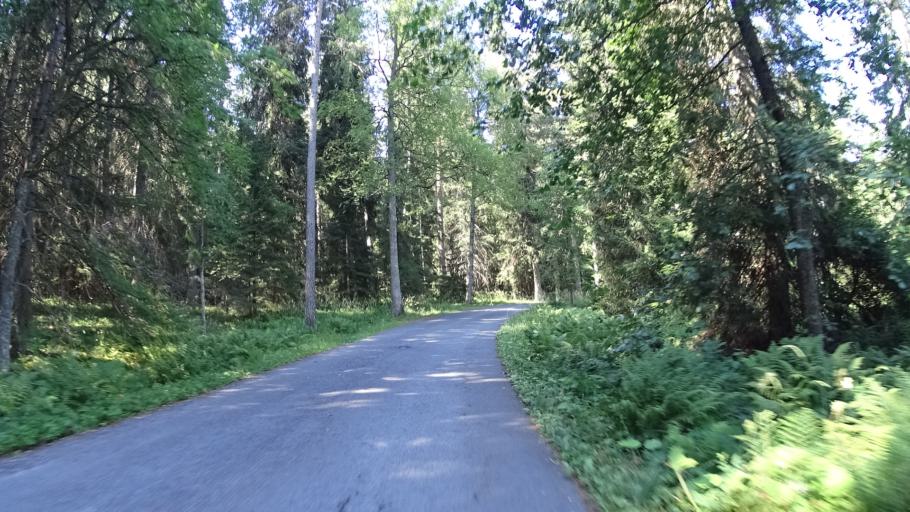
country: FI
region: Haeme
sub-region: Haemeenlinna
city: Haemeenlinna
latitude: 61.0213
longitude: 24.4661
